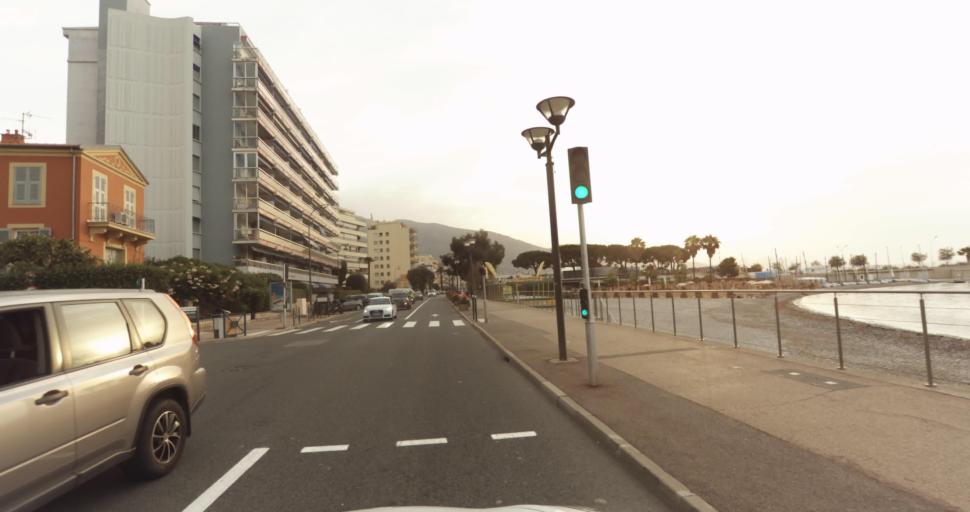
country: FR
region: Provence-Alpes-Cote d'Azur
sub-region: Departement des Alpes-Maritimes
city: Roquebrune-Cap-Martin
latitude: 43.7632
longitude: 7.4857
